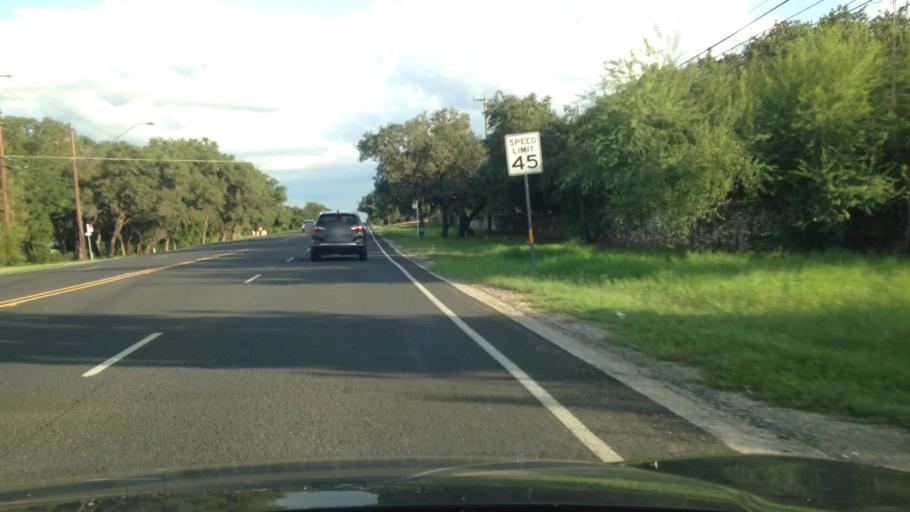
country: US
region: Texas
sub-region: Bexar County
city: Shavano Park
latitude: 29.5838
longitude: -98.5526
